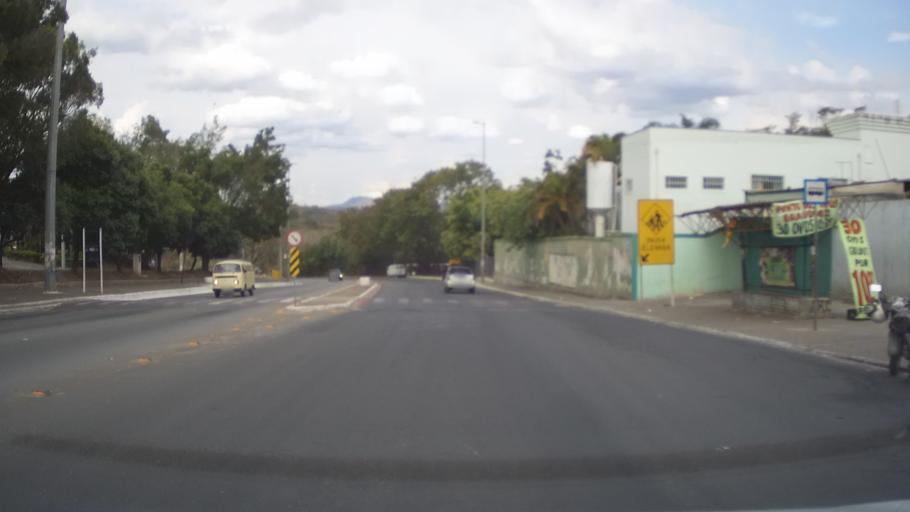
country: BR
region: Minas Gerais
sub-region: Belo Horizonte
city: Belo Horizonte
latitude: -19.8754
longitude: -43.8955
